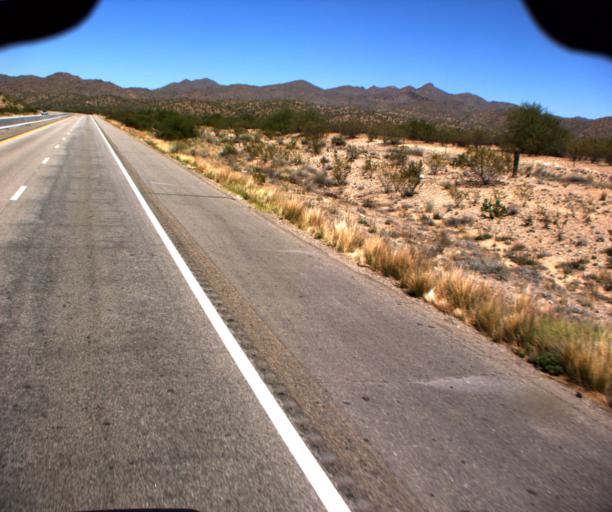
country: US
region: Arizona
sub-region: Yavapai County
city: Bagdad
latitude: 34.3746
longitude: -113.1900
